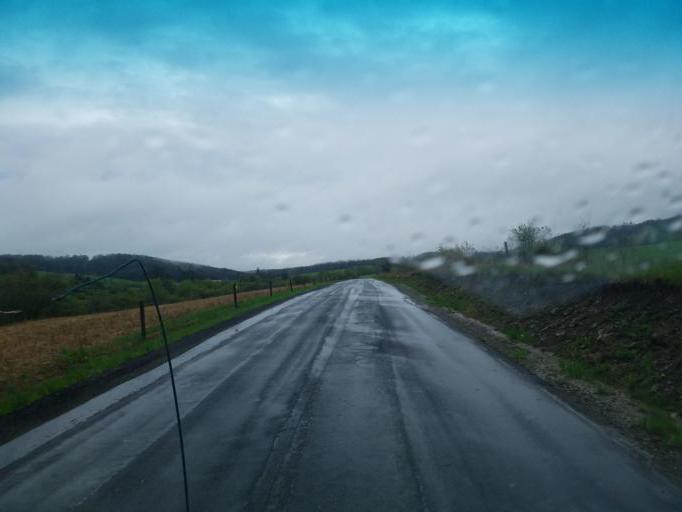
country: US
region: Pennsylvania
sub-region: Tioga County
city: Westfield
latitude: 41.9673
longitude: -77.6558
